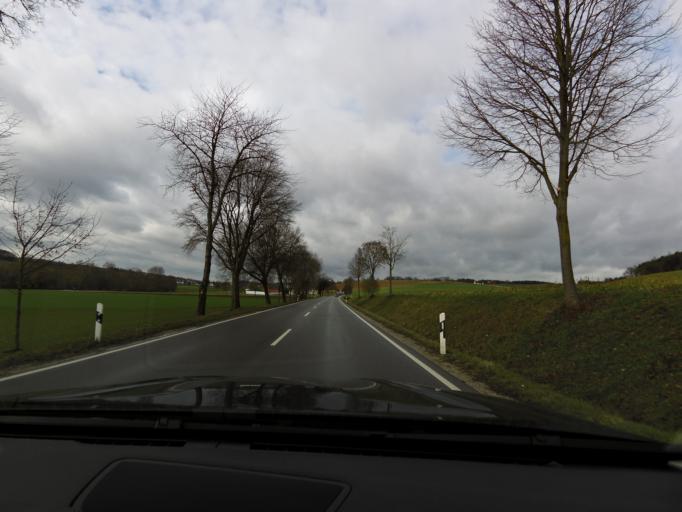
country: DE
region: Bavaria
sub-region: Lower Bavaria
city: Weihmichl
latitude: 48.5892
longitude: 12.0433
